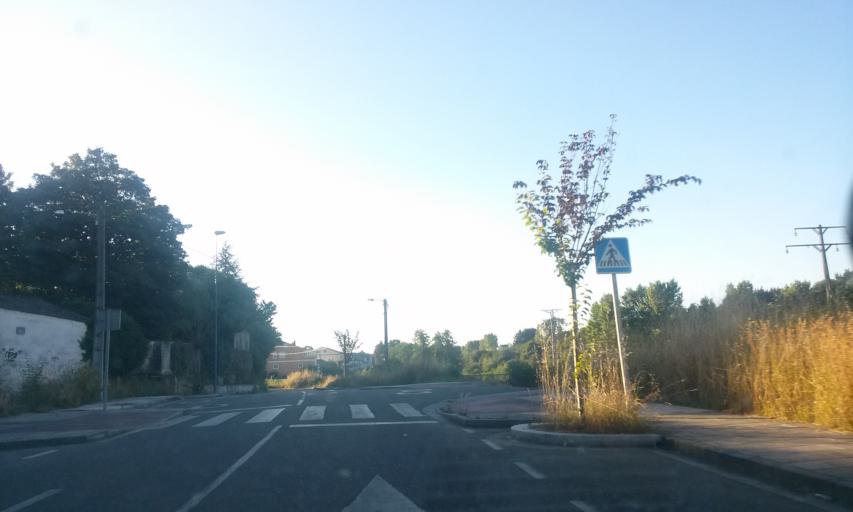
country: ES
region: Galicia
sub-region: Provincia de Lugo
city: Lugo
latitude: 43.0236
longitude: -7.5578
